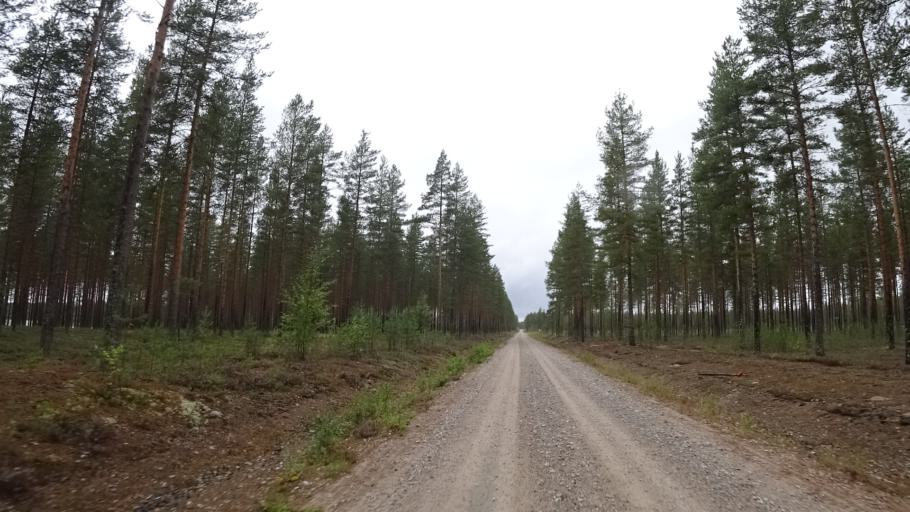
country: FI
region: North Karelia
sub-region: Pielisen Karjala
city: Lieksa
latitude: 63.5259
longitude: 30.0877
